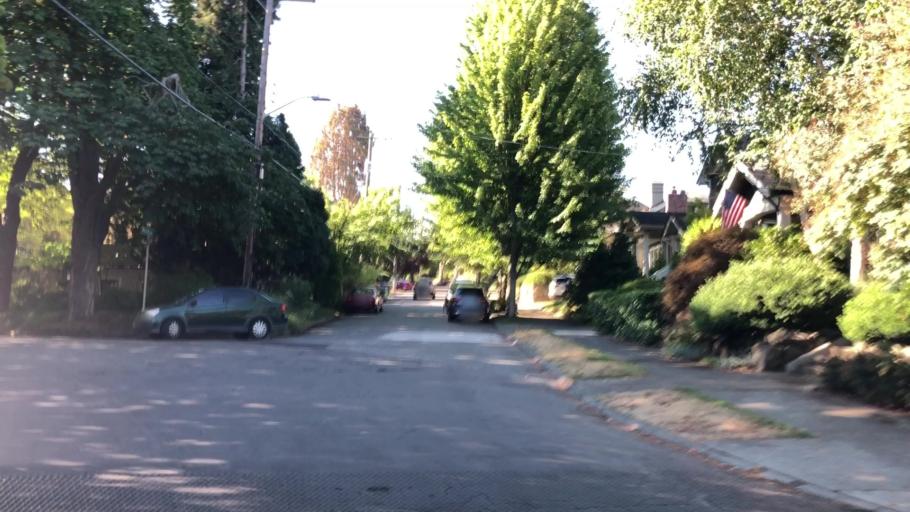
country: US
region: Washington
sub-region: King County
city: Seattle
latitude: 47.6413
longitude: -122.3545
